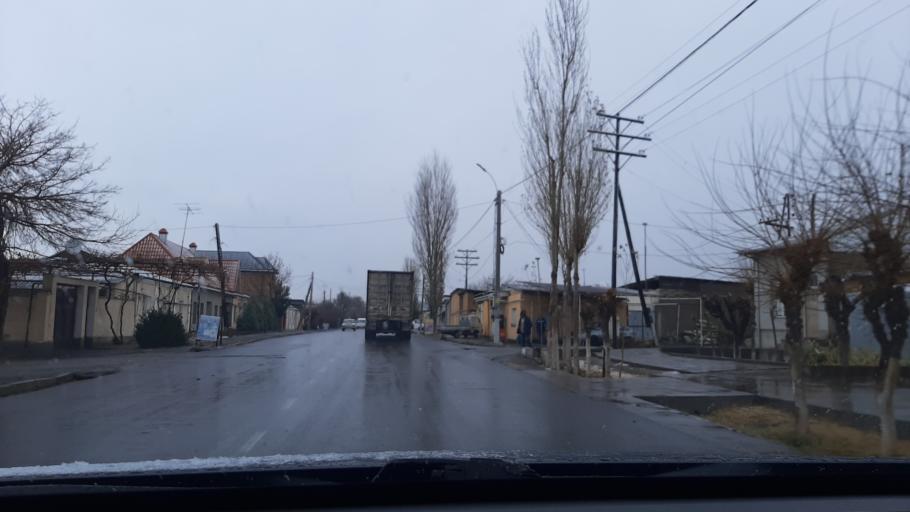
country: TJ
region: Viloyati Sughd
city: Khujand
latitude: 40.2688
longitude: 69.6259
